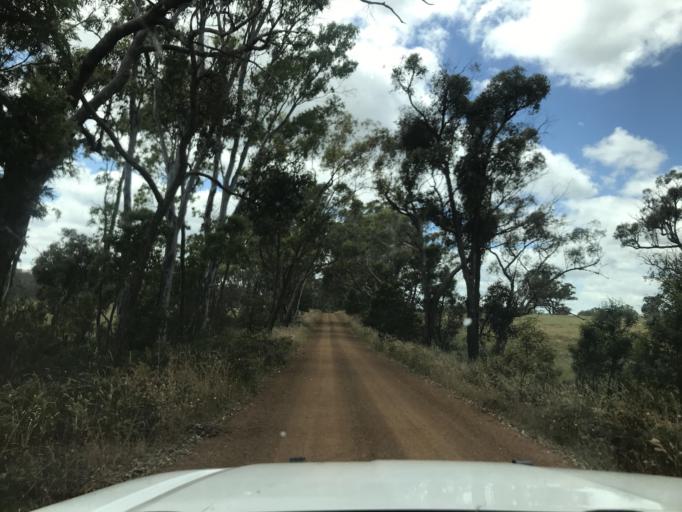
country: AU
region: South Australia
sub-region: Wattle Range
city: Penola
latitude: -37.3717
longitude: 141.2312
